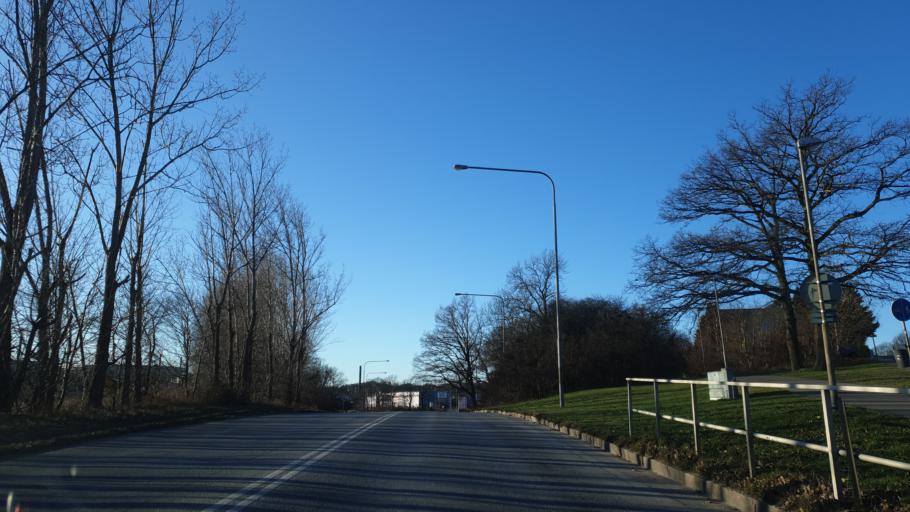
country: SE
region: Blekinge
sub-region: Karlskrona Kommun
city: Rodeby
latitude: 56.2025
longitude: 15.6274
